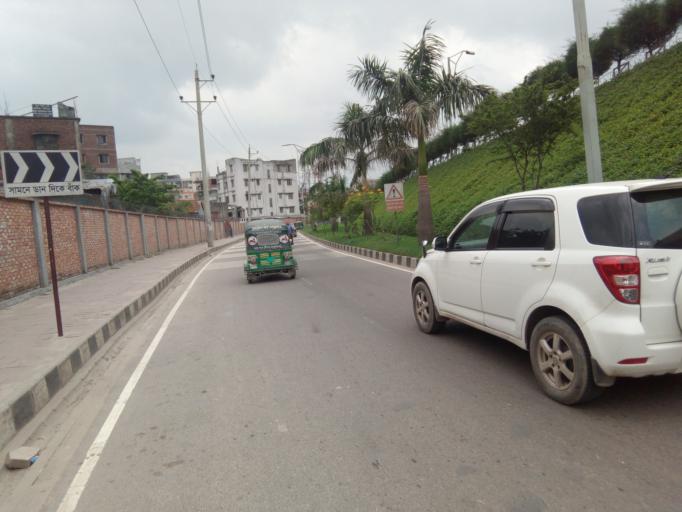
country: BD
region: Dhaka
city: Paltan
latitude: 23.7600
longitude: 90.4106
